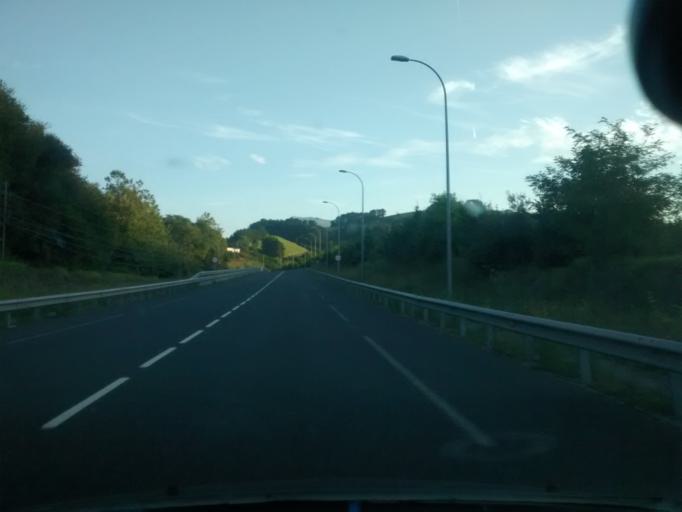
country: ES
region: Basque Country
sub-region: Provincia de Guipuzcoa
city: Zumaia
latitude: 43.2881
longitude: -2.2549
